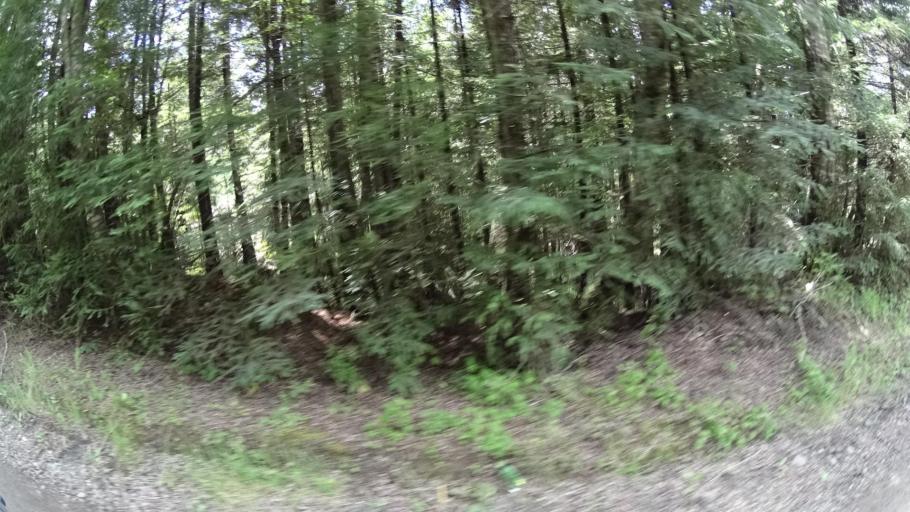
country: US
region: California
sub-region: Humboldt County
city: Blue Lake
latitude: 40.8405
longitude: -123.8952
